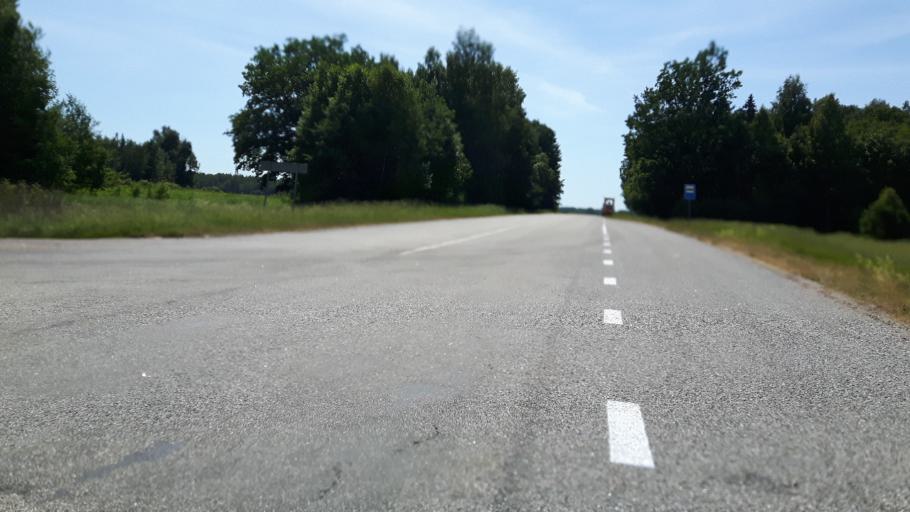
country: LV
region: Aizpute
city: Aizpute
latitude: 56.8080
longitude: 21.7067
